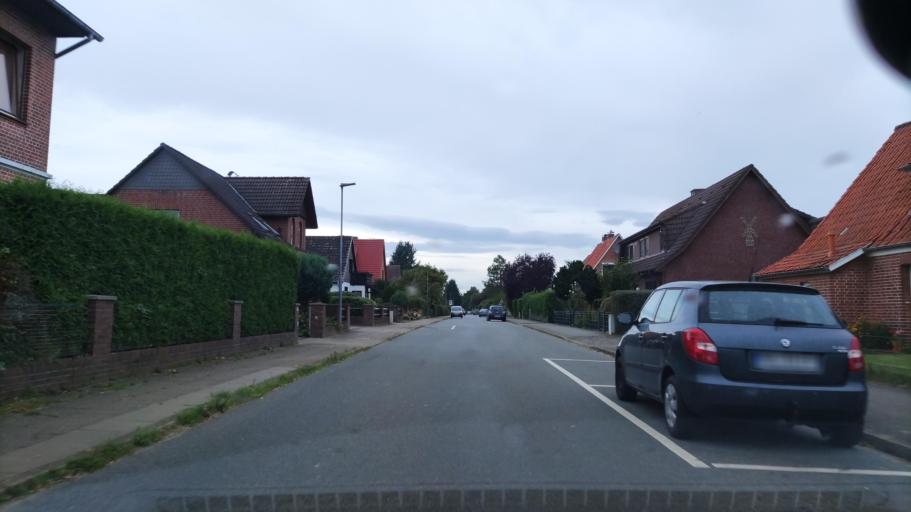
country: DE
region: Schleswig-Holstein
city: Grande
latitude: 53.5808
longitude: 10.3856
